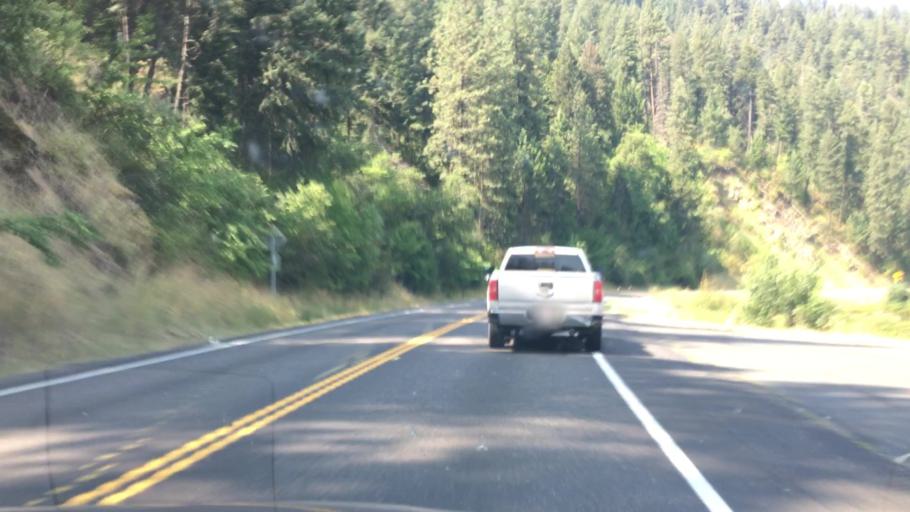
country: US
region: Idaho
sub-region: Clearwater County
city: Orofino
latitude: 46.4897
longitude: -116.4514
